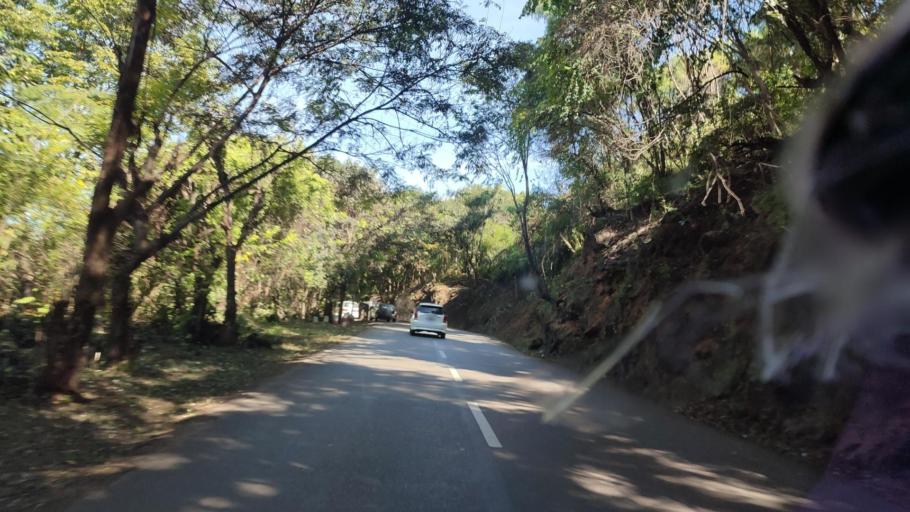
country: MM
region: Shan
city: Taunggyi
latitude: 20.8116
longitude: 97.0316
